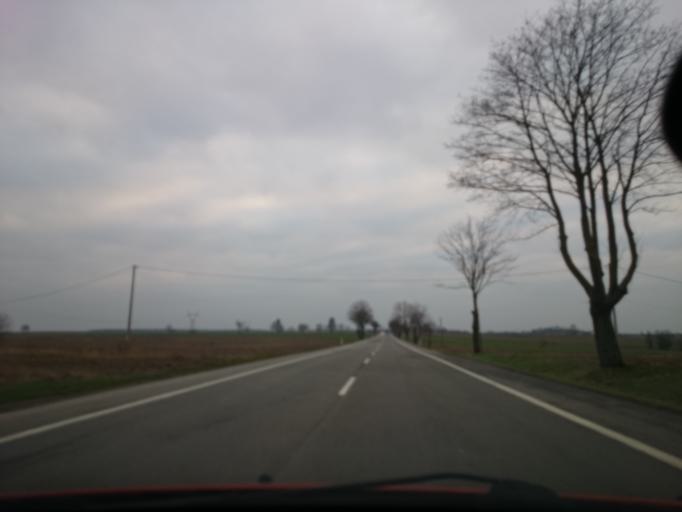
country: PL
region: Opole Voivodeship
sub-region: Powiat nyski
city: Lambinowice
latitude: 50.6038
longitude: 17.5464
